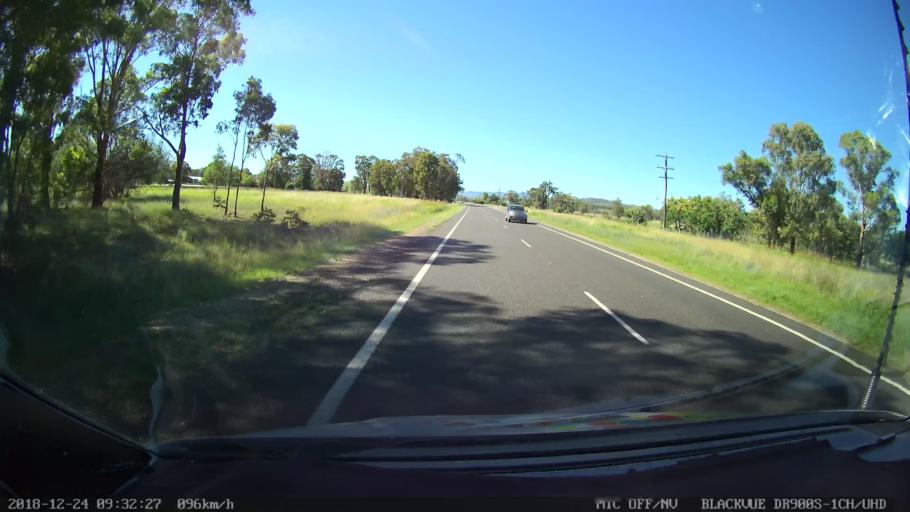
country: AU
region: New South Wales
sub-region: Liverpool Plains
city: Quirindi
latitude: -31.5904
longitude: 150.7025
